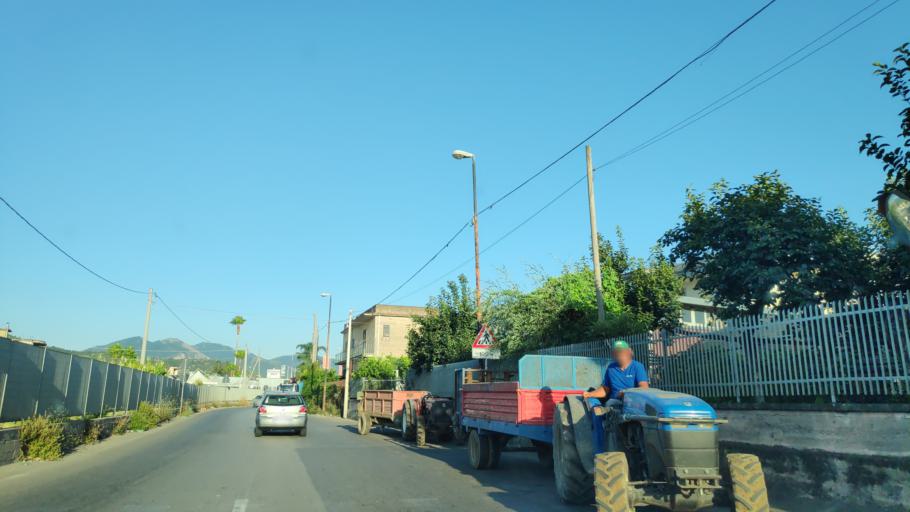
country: IT
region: Campania
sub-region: Provincia di Salerno
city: Pagani
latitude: 40.7637
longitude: 14.6109
